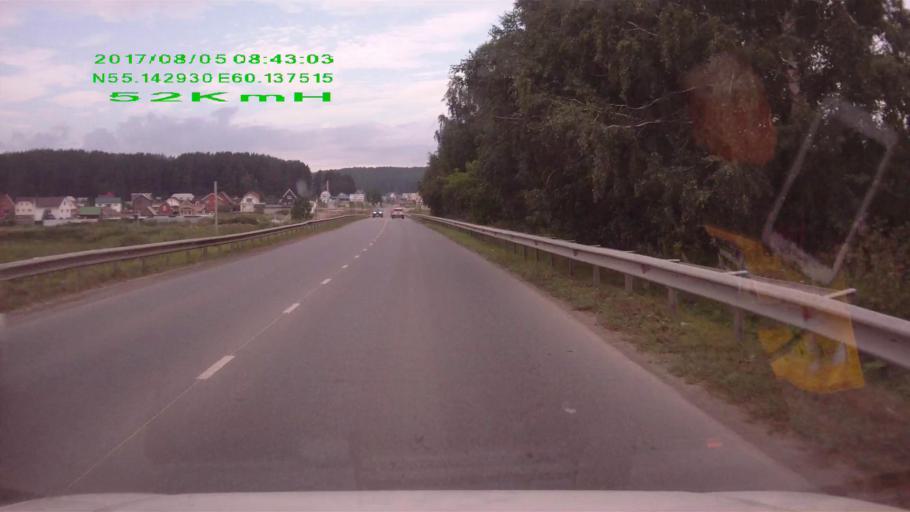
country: RU
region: Chelyabinsk
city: Turgoyak
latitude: 55.1429
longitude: 60.1371
